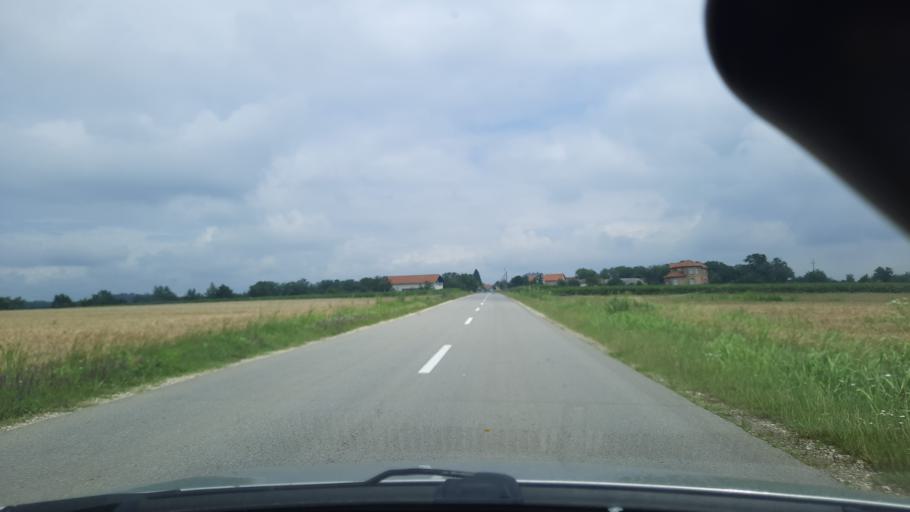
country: RS
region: Central Serbia
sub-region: Branicevski Okrug
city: Malo Crnice
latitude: 44.5803
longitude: 21.3898
